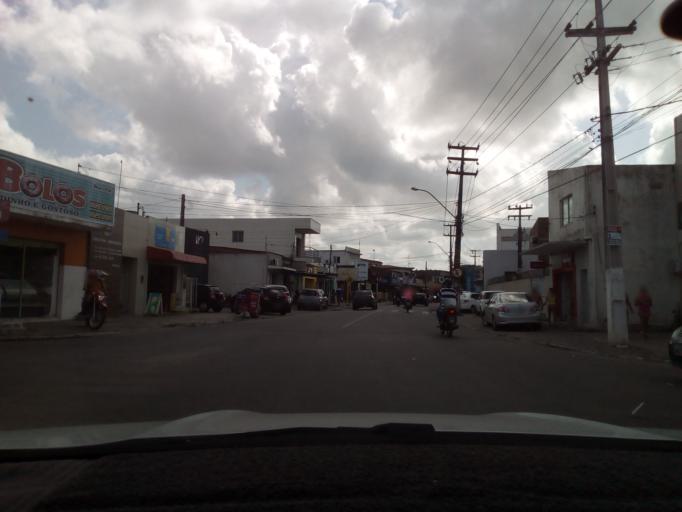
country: BR
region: Paraiba
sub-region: Bayeux
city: Bayeux
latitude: -7.1261
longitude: -34.9291
